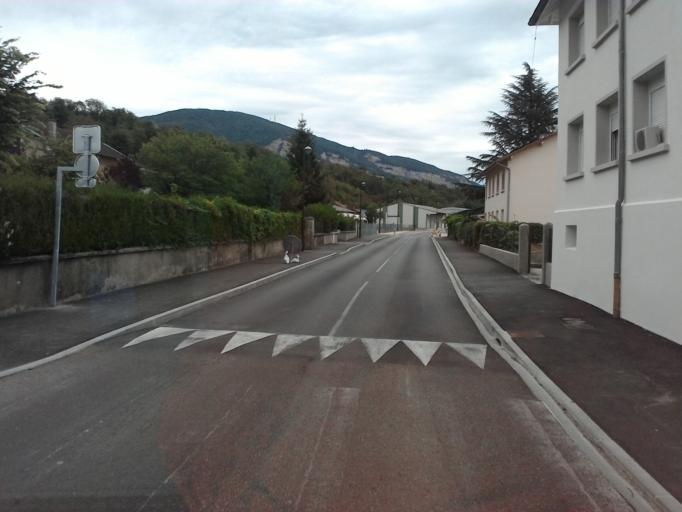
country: FR
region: Rhone-Alpes
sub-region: Departement de l'Ain
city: Sault-Brenaz
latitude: 45.8532
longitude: 5.4134
